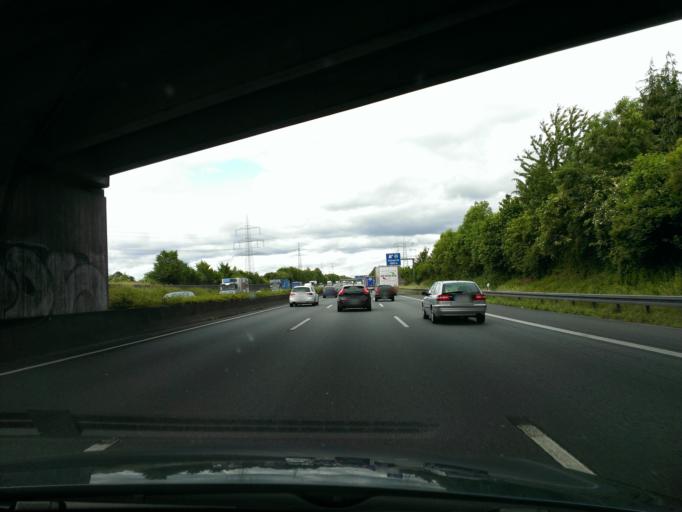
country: DE
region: North Rhine-Westphalia
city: Schwerte
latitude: 51.4611
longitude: 7.5747
